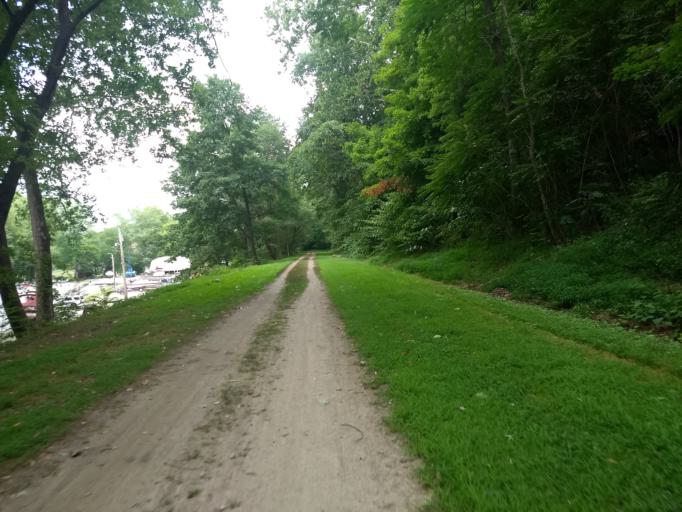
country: US
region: Pennsylvania
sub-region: Armstrong County
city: Freeport
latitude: 40.6438
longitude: -79.6860
